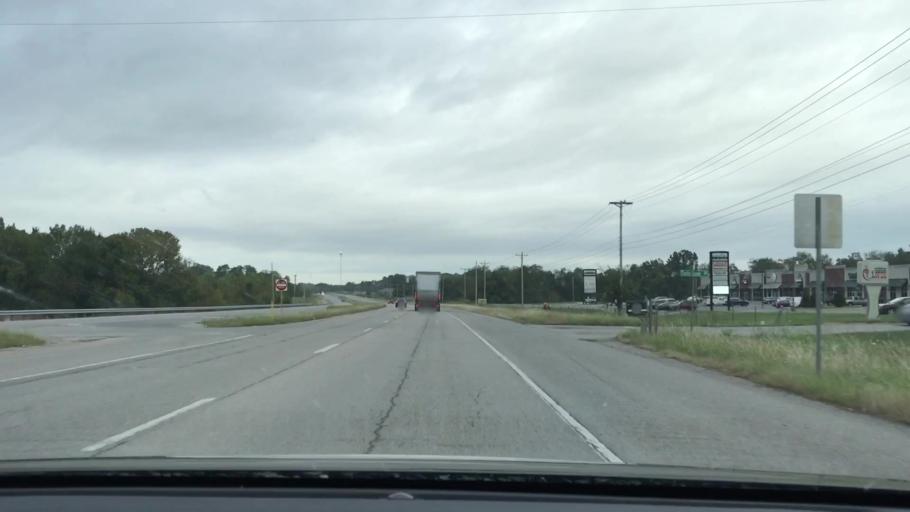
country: US
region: Kentucky
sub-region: Christian County
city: Hopkinsville
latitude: 36.8240
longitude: -87.5076
